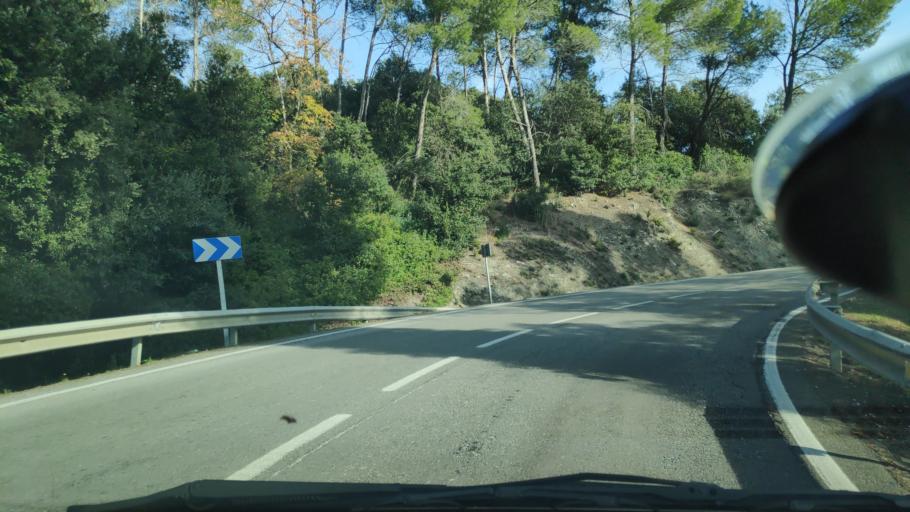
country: ES
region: Catalonia
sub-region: Provincia de Barcelona
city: Matadepera
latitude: 41.5970
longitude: 2.0426
